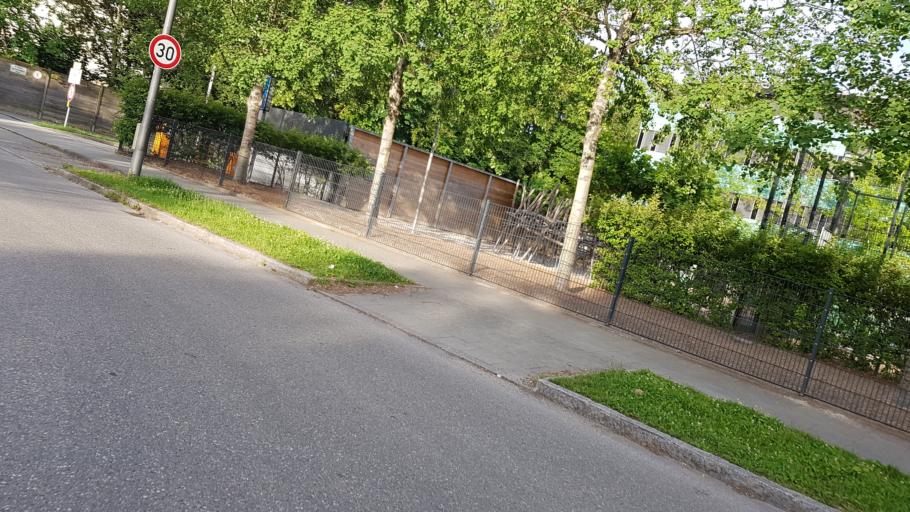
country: DE
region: Bavaria
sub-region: Upper Bavaria
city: Unterhaching
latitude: 48.0910
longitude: 11.6307
